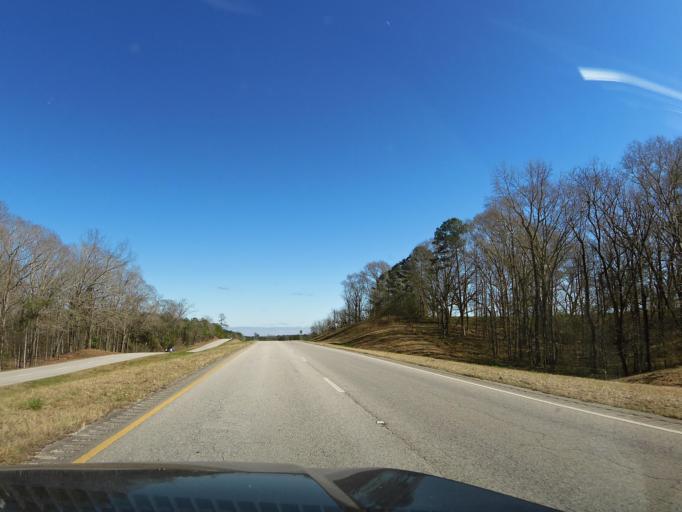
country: US
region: Alabama
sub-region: Bullock County
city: Union Springs
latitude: 32.1461
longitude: -85.6410
